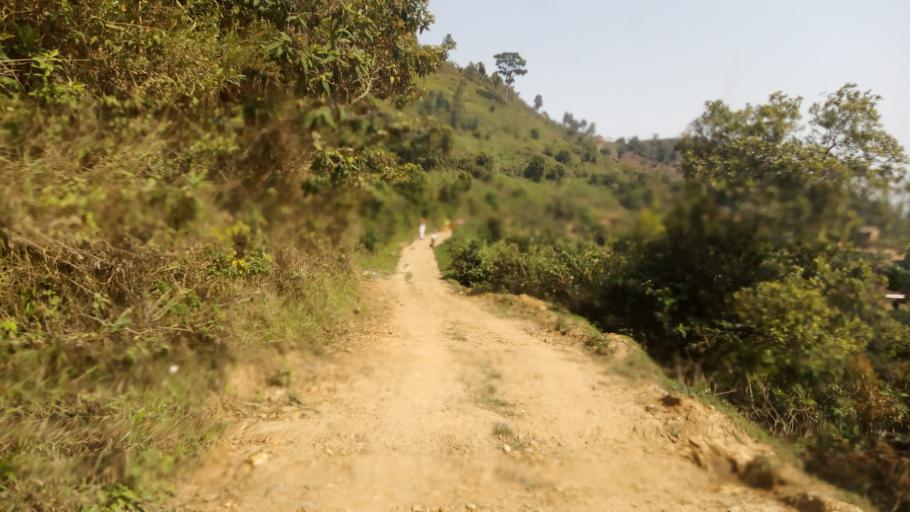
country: UG
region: Western Region
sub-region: Kisoro District
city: Kisoro
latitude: -1.1123
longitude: 29.5938
